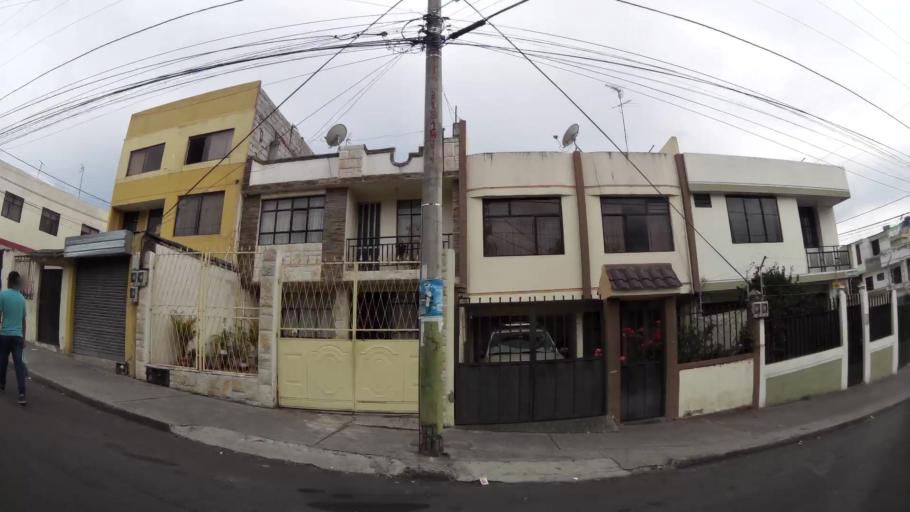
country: EC
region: Tungurahua
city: Ambato
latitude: -1.2618
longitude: -78.6338
